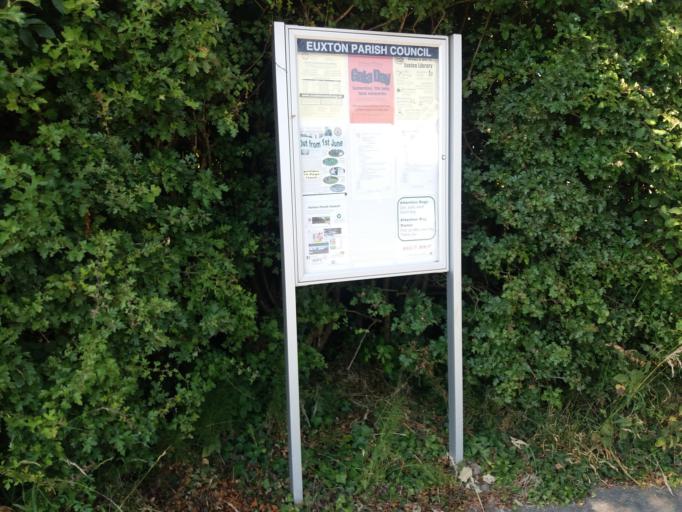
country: GB
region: England
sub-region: Lancashire
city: Euxton
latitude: 53.6716
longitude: -2.6703
